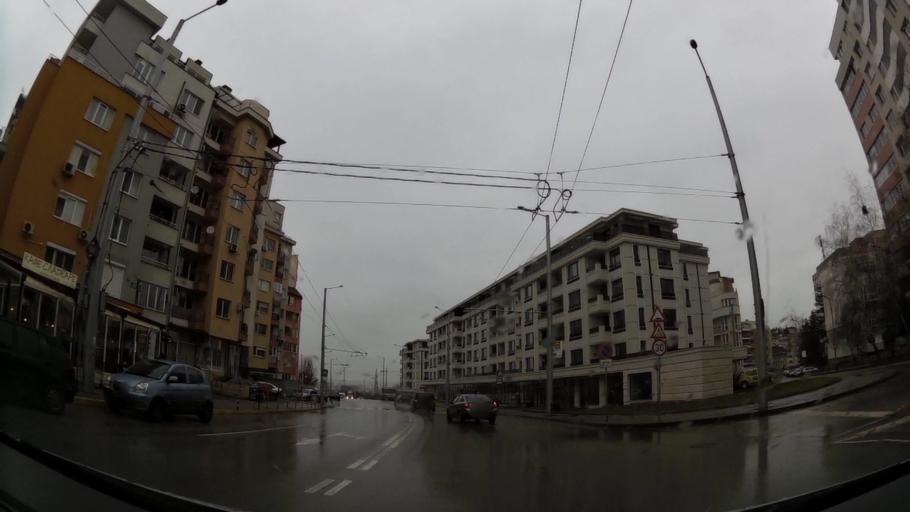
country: BG
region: Sofia-Capital
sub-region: Stolichna Obshtina
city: Sofia
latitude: 42.6464
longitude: 23.3682
